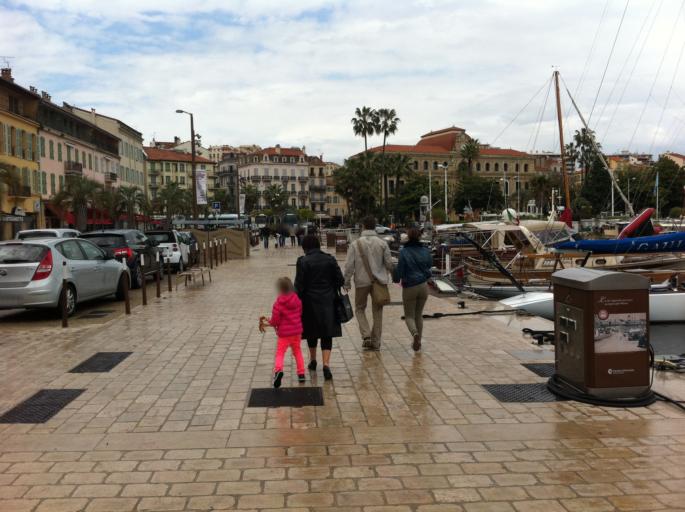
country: FR
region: Provence-Alpes-Cote d'Azur
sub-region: Departement des Alpes-Maritimes
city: Cannes
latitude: 43.5498
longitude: 7.0124
